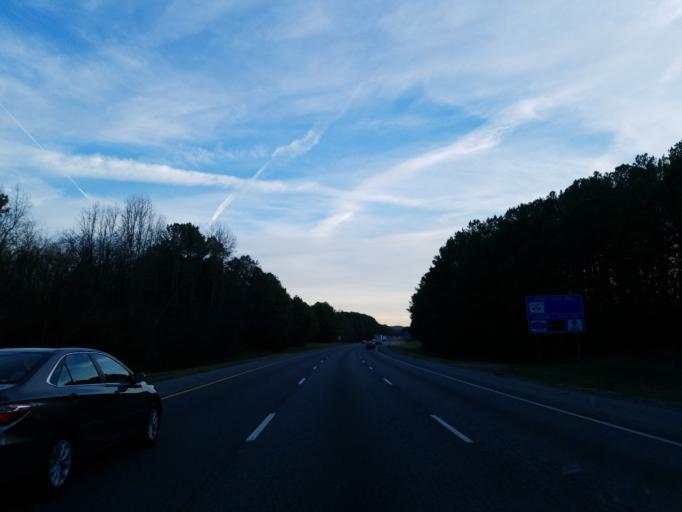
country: US
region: Georgia
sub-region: Bartow County
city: Cartersville
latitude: 34.2288
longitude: -84.7541
